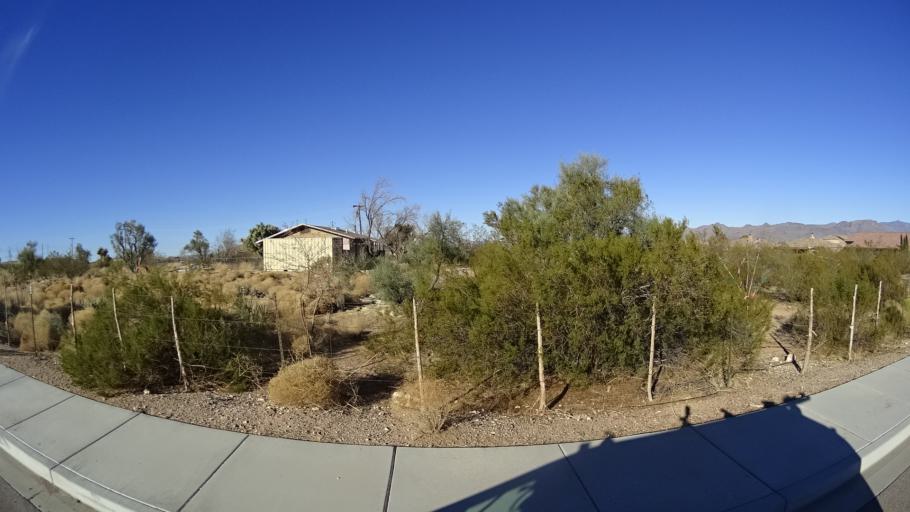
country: US
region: Arizona
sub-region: Mohave County
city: Kingman
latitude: 35.1835
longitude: -113.9983
